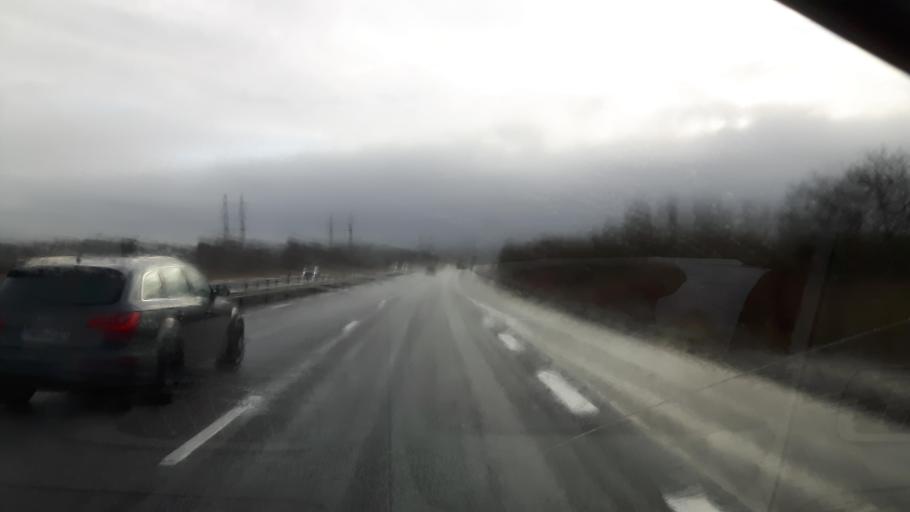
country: SE
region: Halland
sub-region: Kungsbacka Kommun
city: Kungsbacka
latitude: 57.4709
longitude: 12.0600
